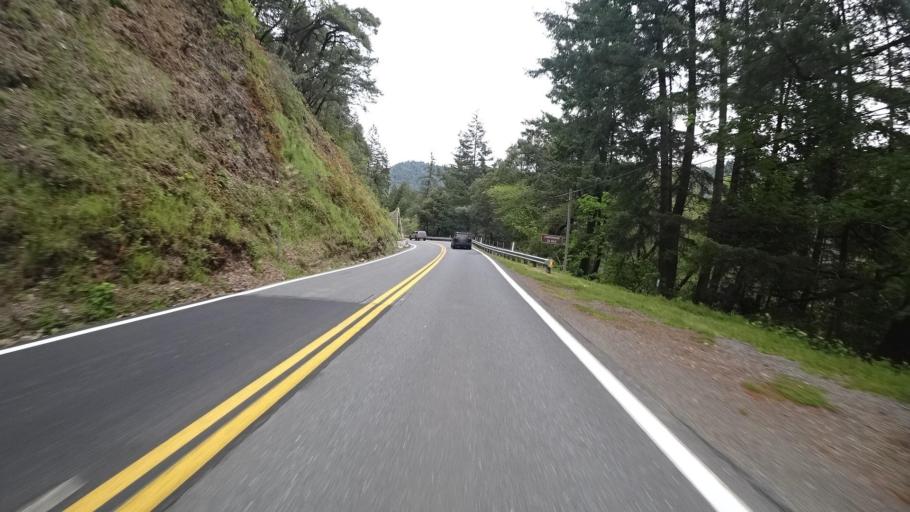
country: US
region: California
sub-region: Humboldt County
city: Willow Creek
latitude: 41.0169
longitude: -123.6370
